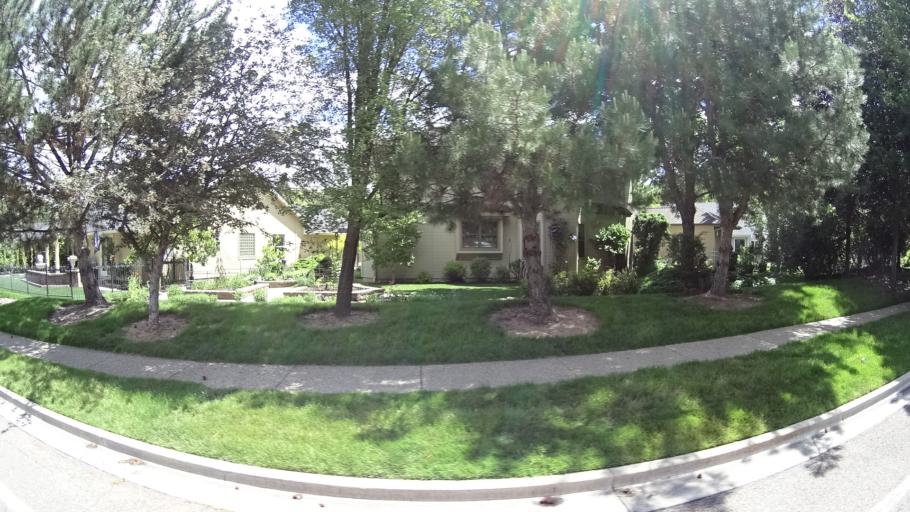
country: US
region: Idaho
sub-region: Ada County
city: Boise
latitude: 43.5843
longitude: -116.1667
